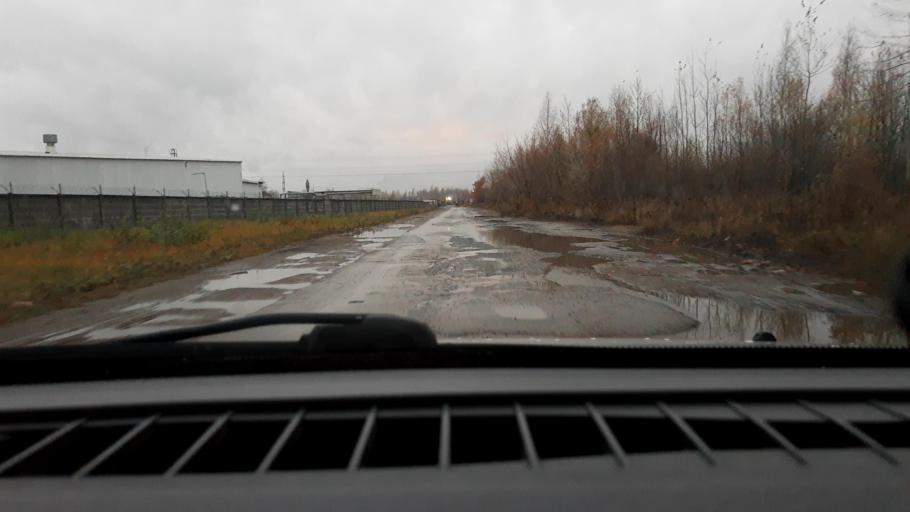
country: RU
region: Nizjnij Novgorod
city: Gorbatovka
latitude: 56.2708
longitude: 43.8535
